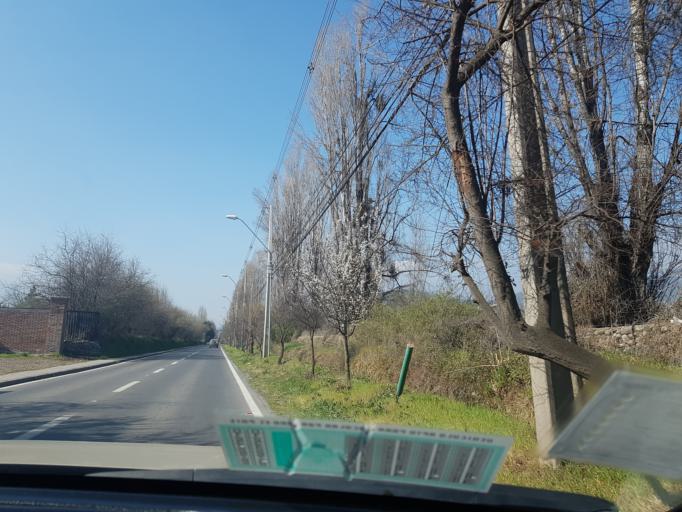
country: CL
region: Santiago Metropolitan
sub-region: Provincia de Cordillera
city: Puente Alto
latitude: -33.6312
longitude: -70.5616
